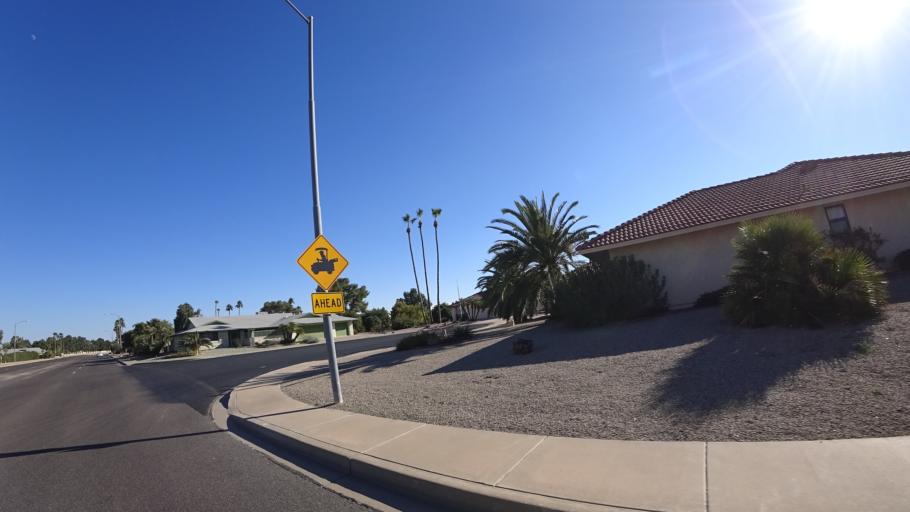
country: US
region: Arizona
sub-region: Maricopa County
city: Sun City West
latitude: 33.6781
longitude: -112.3457
